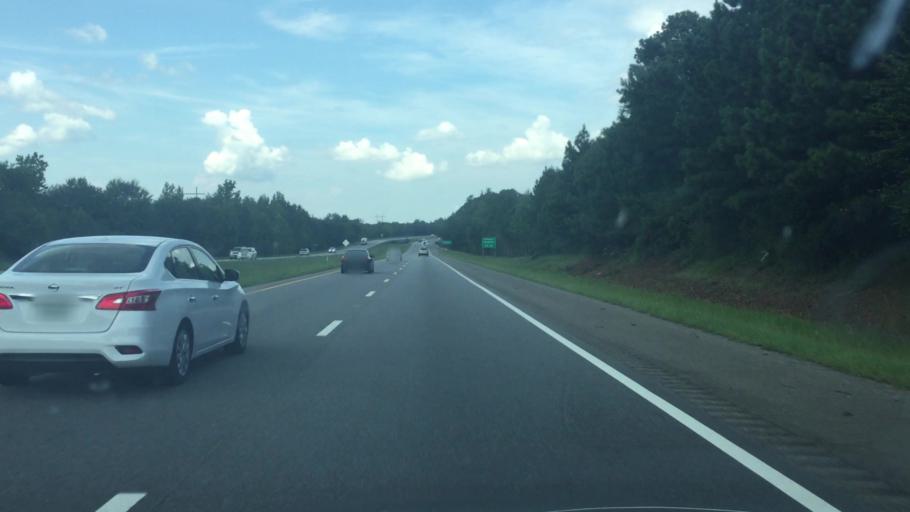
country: US
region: North Carolina
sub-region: Richmond County
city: Hamlet
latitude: 34.8531
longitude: -79.7237
